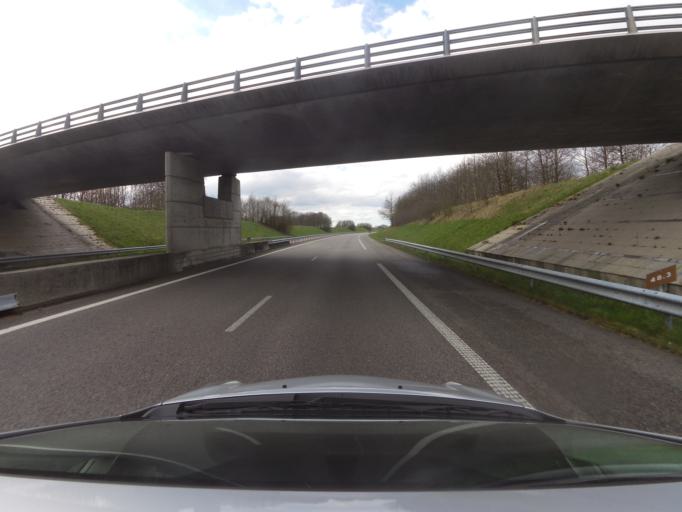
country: FR
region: Haute-Normandie
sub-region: Departement de la Seine-Maritime
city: Nointot
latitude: 49.6032
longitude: 0.4927
